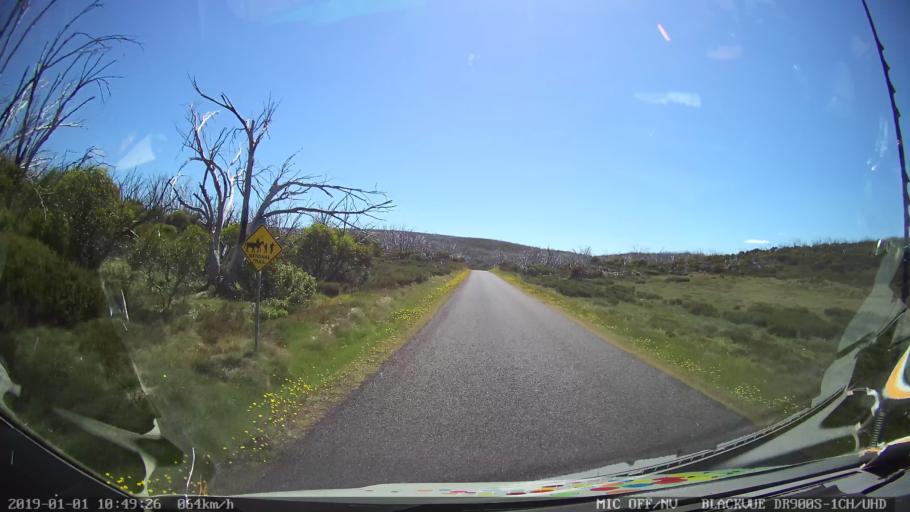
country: AU
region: New South Wales
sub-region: Snowy River
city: Jindabyne
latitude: -36.0347
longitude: 148.3704
